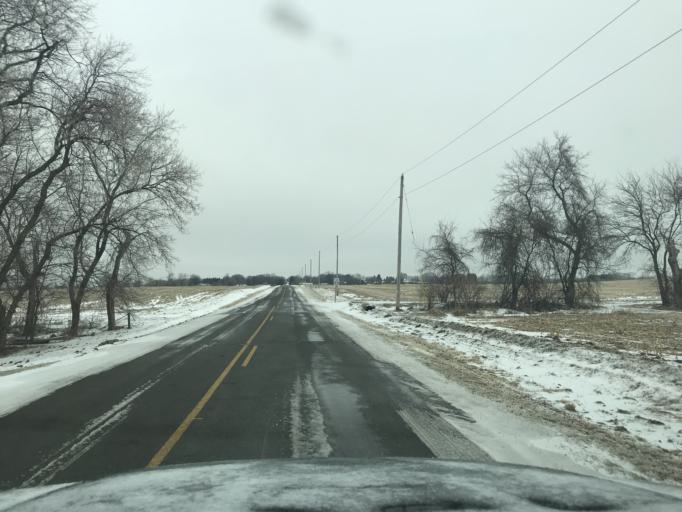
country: US
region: Wisconsin
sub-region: Dane County
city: Cottage Grove
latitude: 43.0966
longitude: -89.2296
